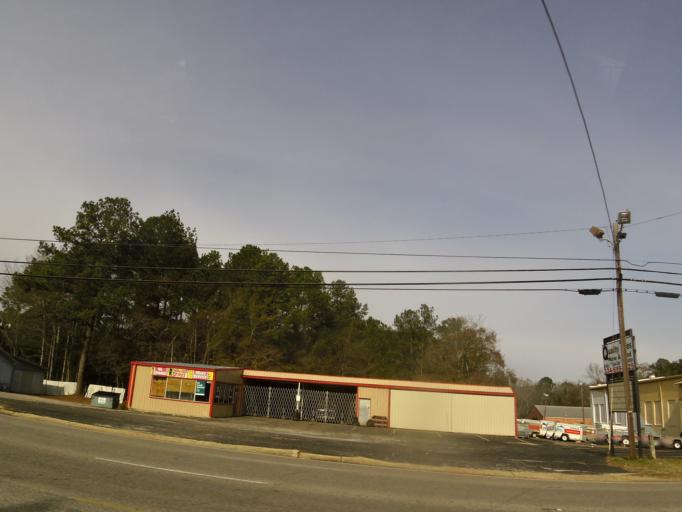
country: US
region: Alabama
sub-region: Houston County
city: Dothan
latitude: 31.2390
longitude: -85.4041
